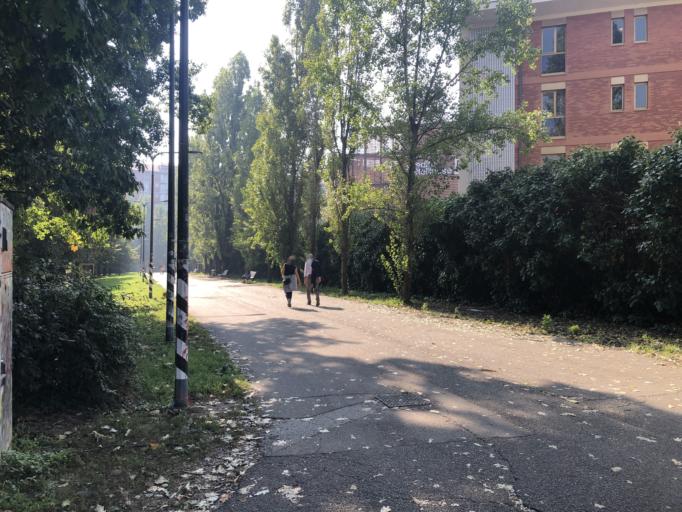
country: IT
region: Lombardy
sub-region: Citta metropolitana di Milano
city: Sesto San Giovanni
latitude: 45.4928
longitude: 9.2458
